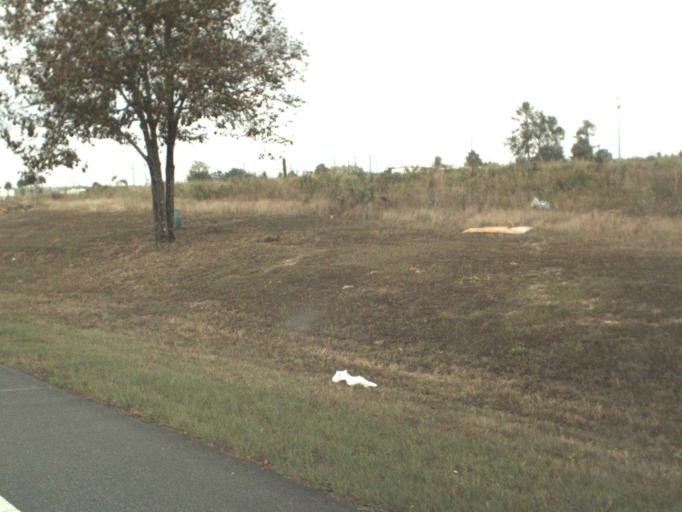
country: US
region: Florida
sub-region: Leon County
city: Tallahassee
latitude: 30.3984
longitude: -84.3508
